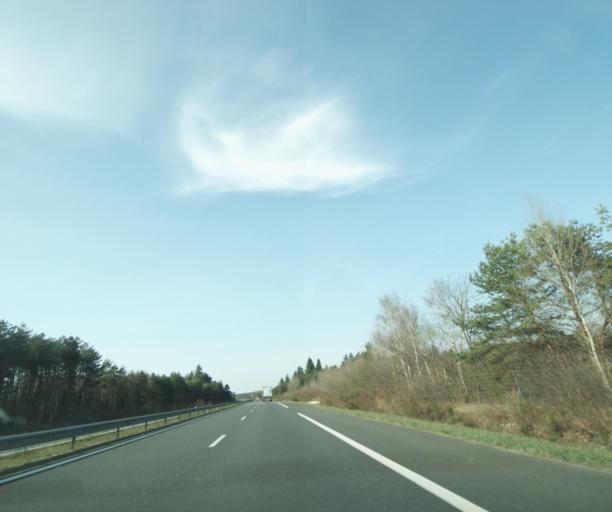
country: FR
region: Centre
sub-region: Departement du Loir-et-Cher
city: Chaumont-sur-Tharonne
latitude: 47.6272
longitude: 1.9584
